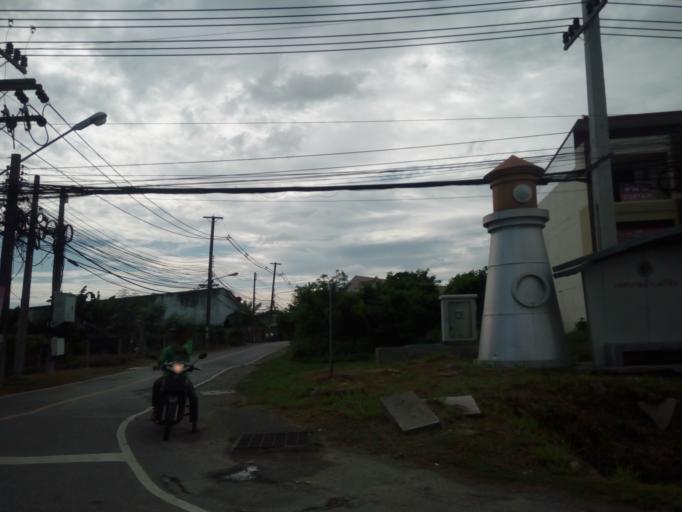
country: TH
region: Phuket
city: Mueang Phuket
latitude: 7.8458
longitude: 98.3829
